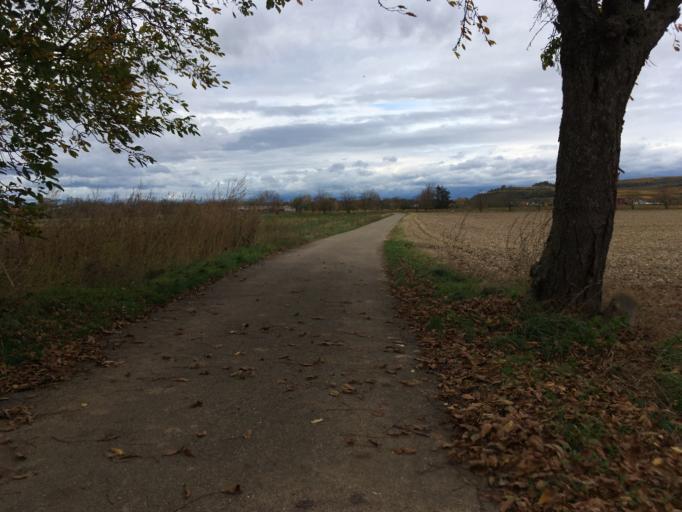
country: DE
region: Baden-Wuerttemberg
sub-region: Freiburg Region
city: Sasbach
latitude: 48.1402
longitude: 7.6328
